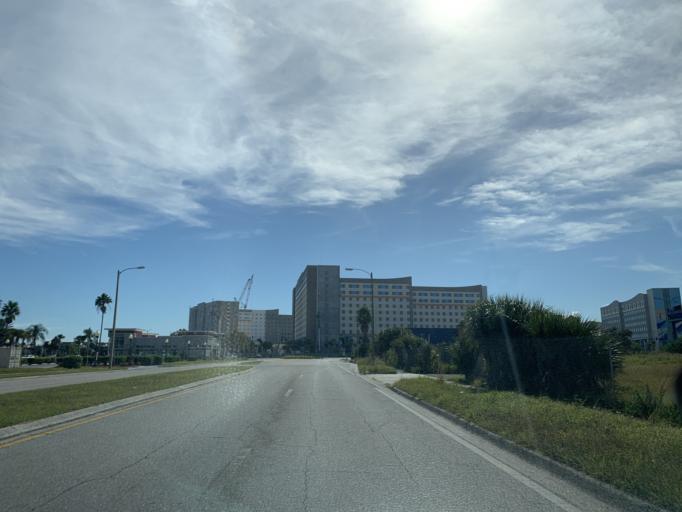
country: US
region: Florida
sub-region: Orange County
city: Tangelo Park
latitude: 28.4639
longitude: -81.4626
